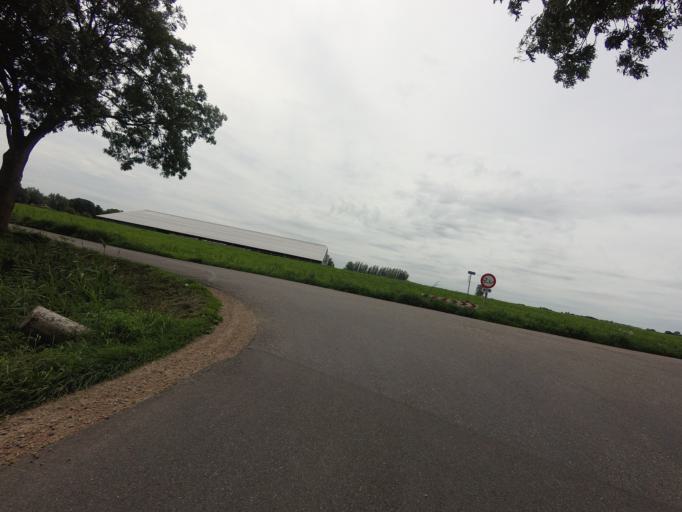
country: NL
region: Utrecht
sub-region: Gemeente De Ronde Venen
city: Mijdrecht
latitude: 52.2436
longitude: 4.8723
